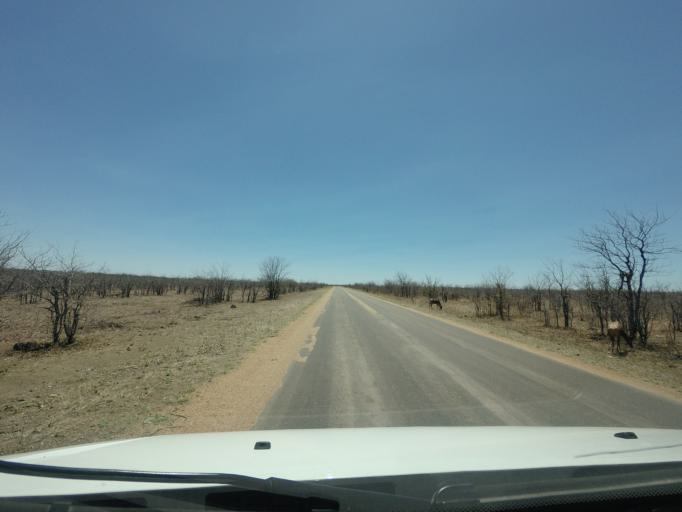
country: ZA
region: Limpopo
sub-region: Mopani District Municipality
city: Phalaborwa
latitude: -23.5724
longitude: 31.4516
